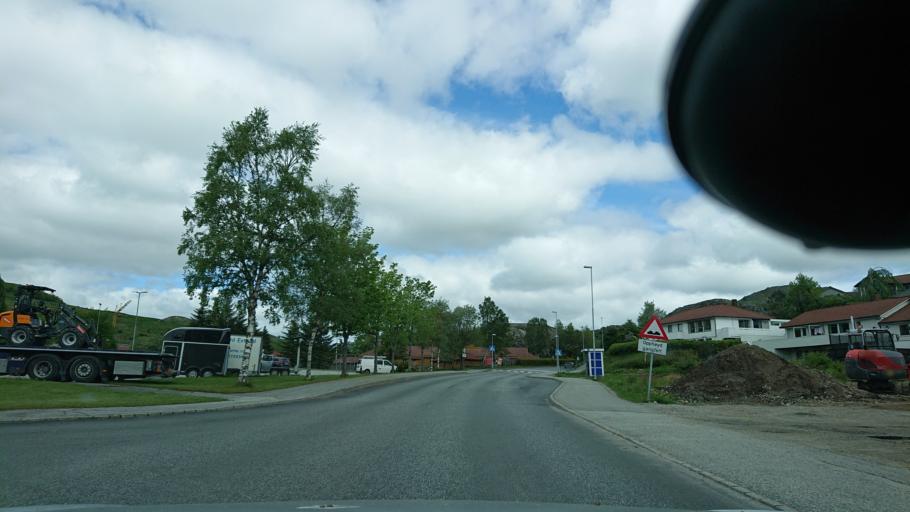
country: NO
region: Rogaland
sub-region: Gjesdal
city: Algard
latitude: 58.7719
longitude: 5.8650
